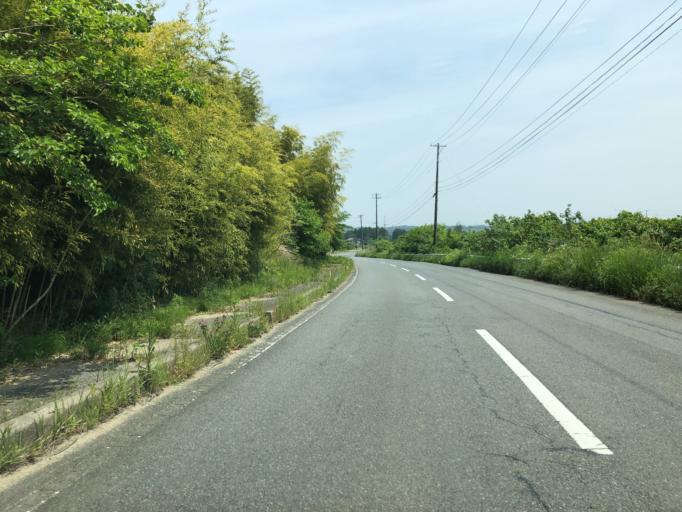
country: JP
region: Fukushima
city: Namie
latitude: 37.5522
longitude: 140.9316
